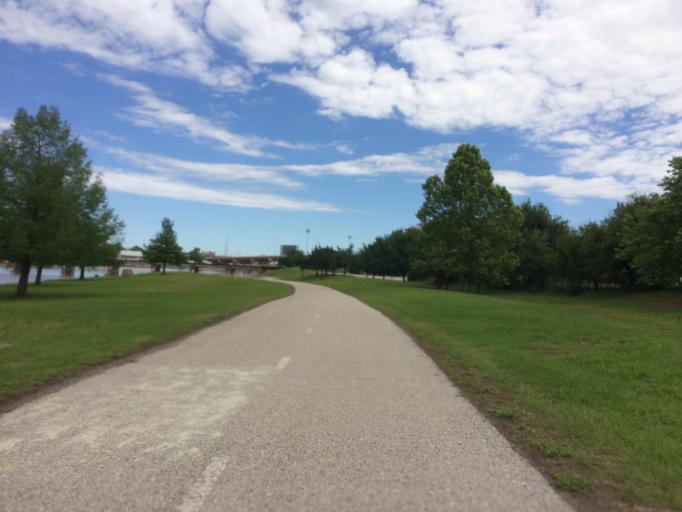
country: US
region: Oklahoma
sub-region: Oklahoma County
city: Oklahoma City
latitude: 35.4537
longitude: -97.5063
